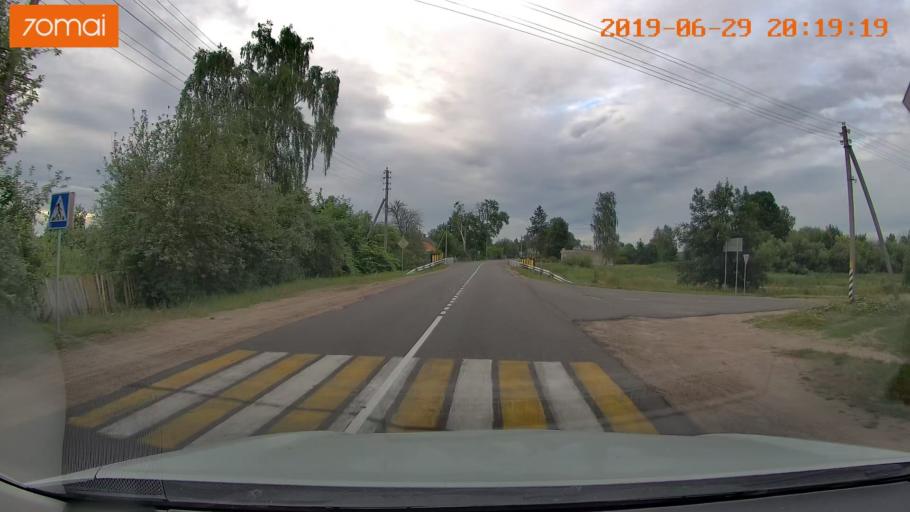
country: BY
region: Brest
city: Asnyezhytsy
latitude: 52.4001
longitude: 26.2437
